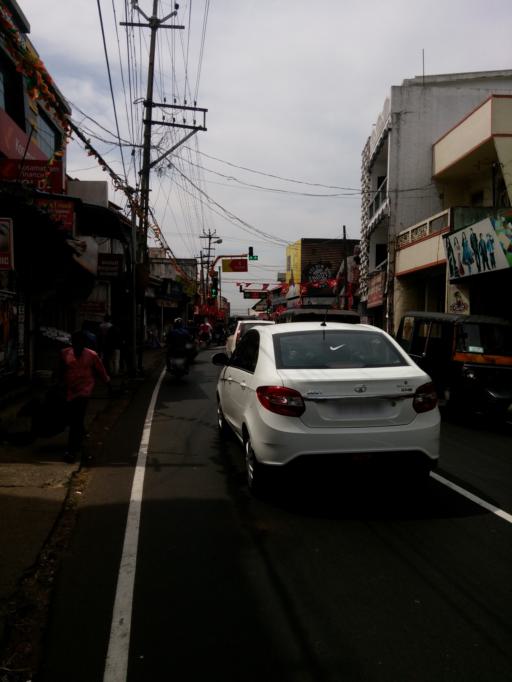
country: IN
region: Kerala
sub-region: Palakkad district
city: Palakkad
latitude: 10.7713
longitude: 76.6610
